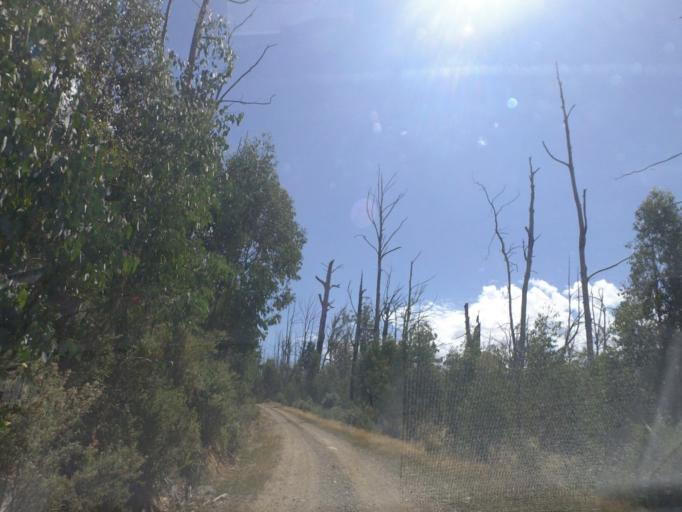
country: AU
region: Victoria
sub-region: Murrindindi
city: Alexandra
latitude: -37.4763
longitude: 145.8393
